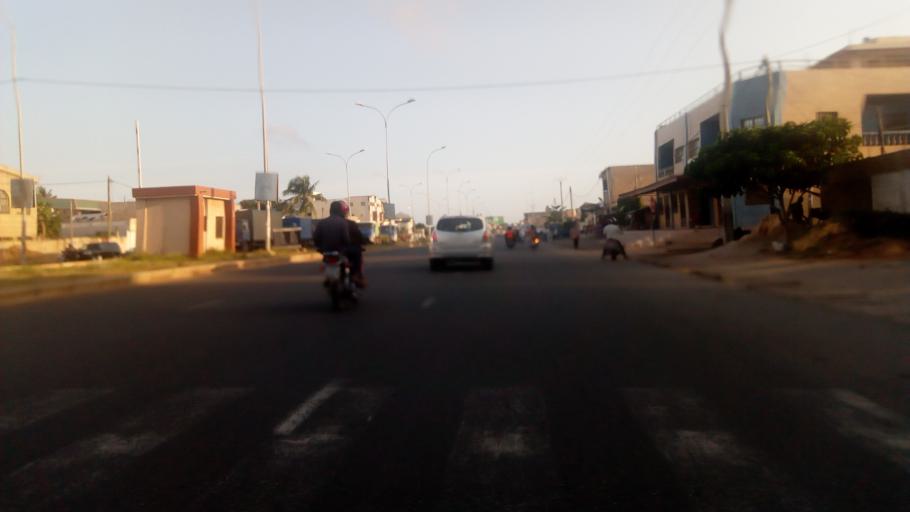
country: TG
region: Maritime
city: Lome
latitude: 6.2060
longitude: 1.1822
